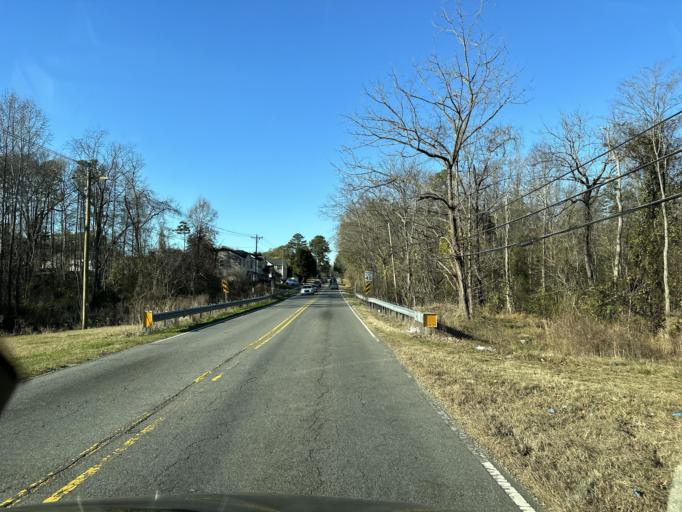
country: US
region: North Carolina
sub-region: Gaston County
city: Mount Holly
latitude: 35.2982
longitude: -80.9343
